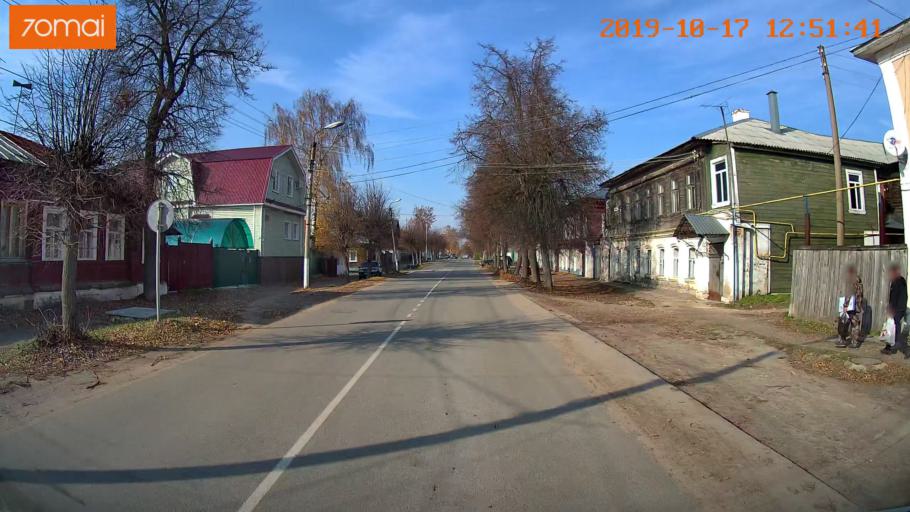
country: RU
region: Rjazan
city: Kasimov
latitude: 54.9414
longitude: 41.3911
